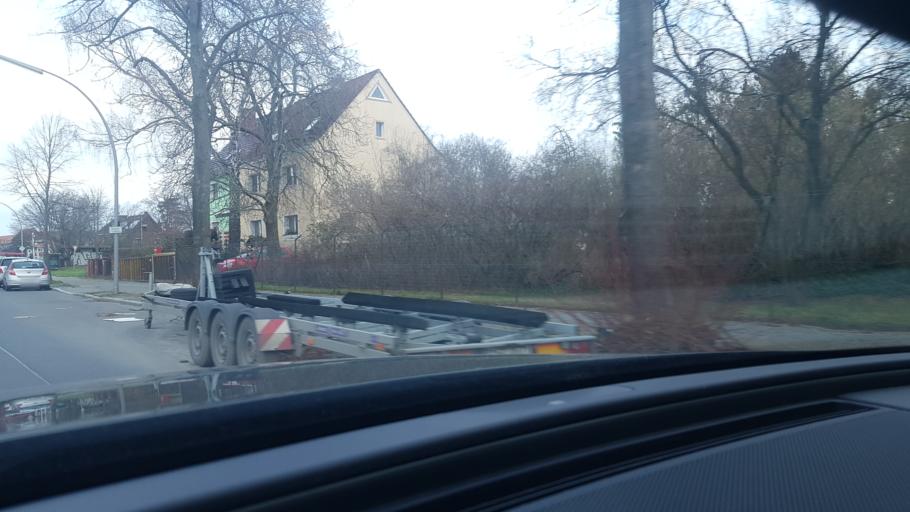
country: DE
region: Berlin
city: Mariendorf
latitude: 52.4213
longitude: 13.3865
